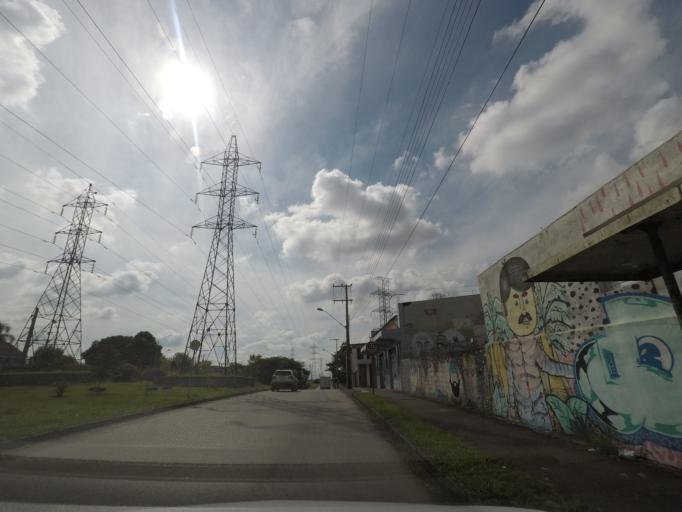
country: BR
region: Parana
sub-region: Pinhais
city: Pinhais
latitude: -25.4823
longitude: -49.2080
